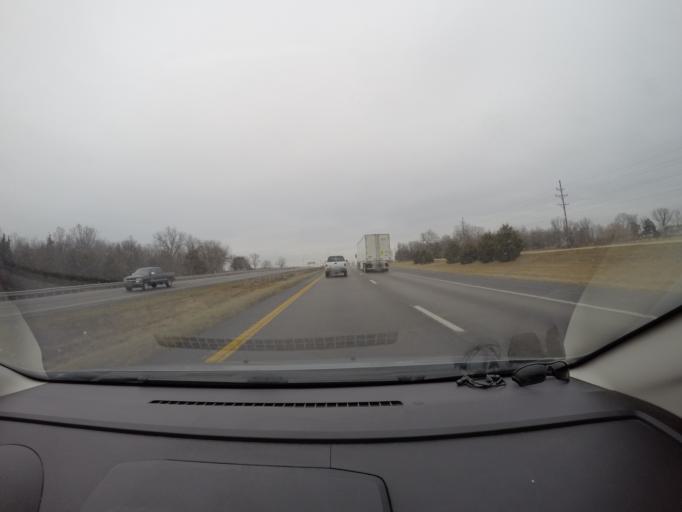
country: US
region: Missouri
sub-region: Warren County
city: Warrenton
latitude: 38.8459
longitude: -91.2382
